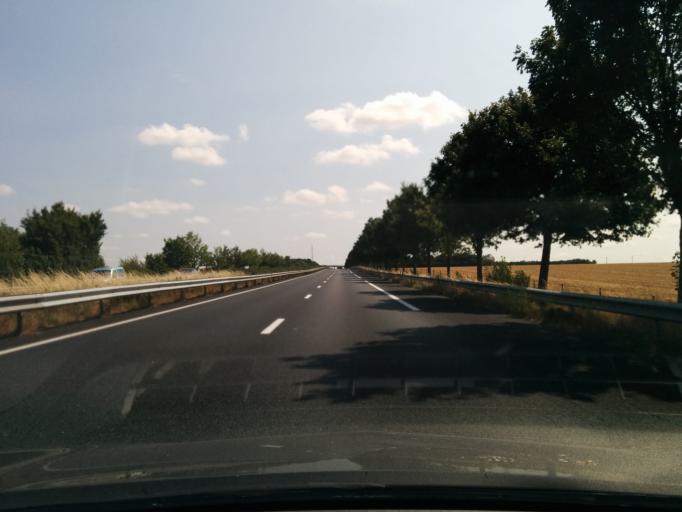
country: FR
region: Centre
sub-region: Departement de l'Indre
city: Vatan
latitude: 47.0007
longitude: 1.7771
